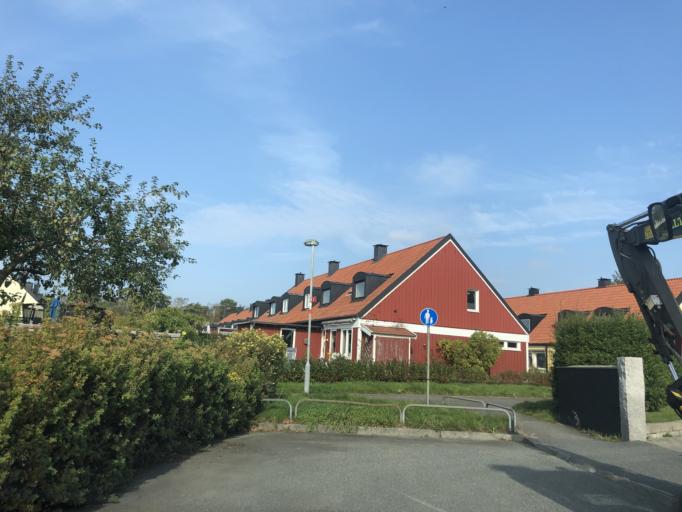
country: SE
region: Vaestra Goetaland
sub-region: Goteborg
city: Majorna
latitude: 57.6453
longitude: 11.8898
